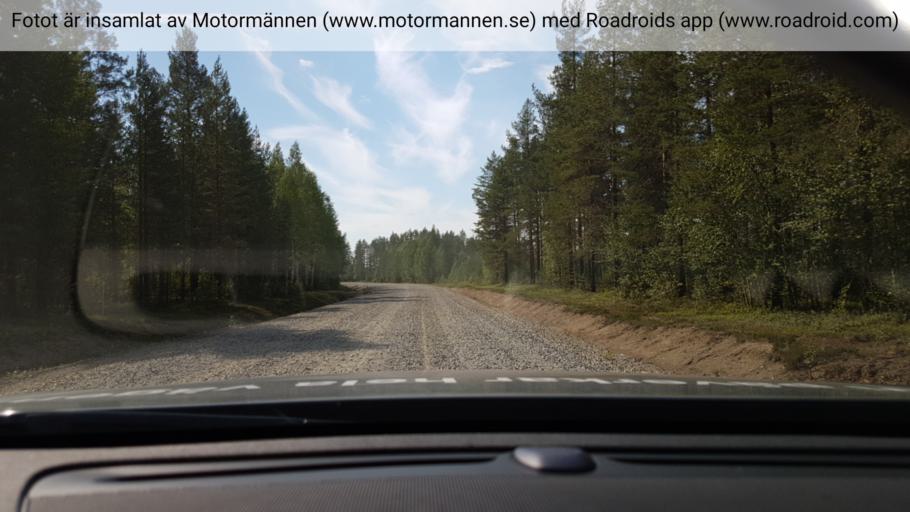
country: SE
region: Vaesterbotten
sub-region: Norsjo Kommun
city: Norsjoe
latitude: 64.6275
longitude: 19.2862
